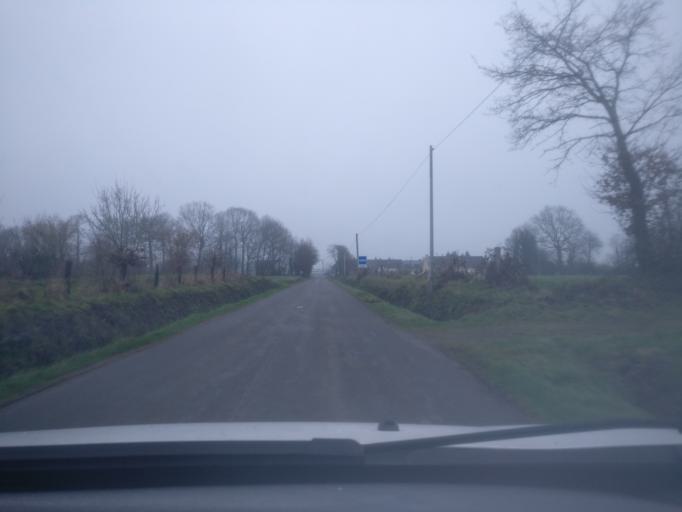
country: FR
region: Brittany
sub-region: Departement d'Ille-et-Vilaine
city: Montreuil-sur-Ille
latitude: 48.3202
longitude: -1.6364
